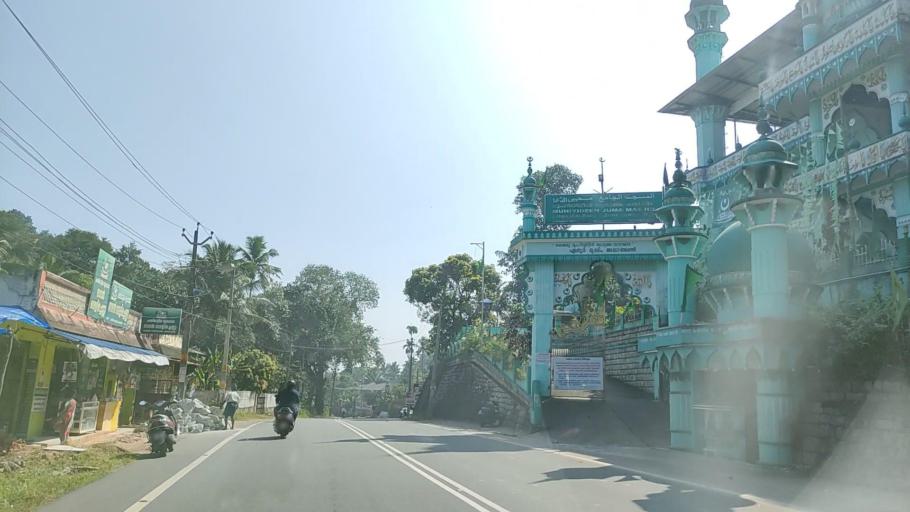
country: IN
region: Kerala
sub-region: Kollam
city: Punalur
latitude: 8.9349
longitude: 76.9499
